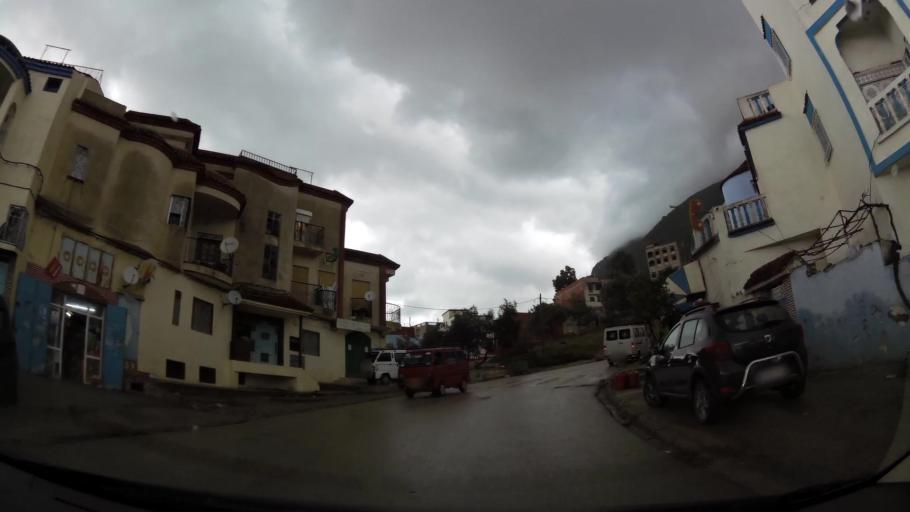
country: MA
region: Tanger-Tetouan
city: Chefchaouene
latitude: 35.1766
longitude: -5.2732
